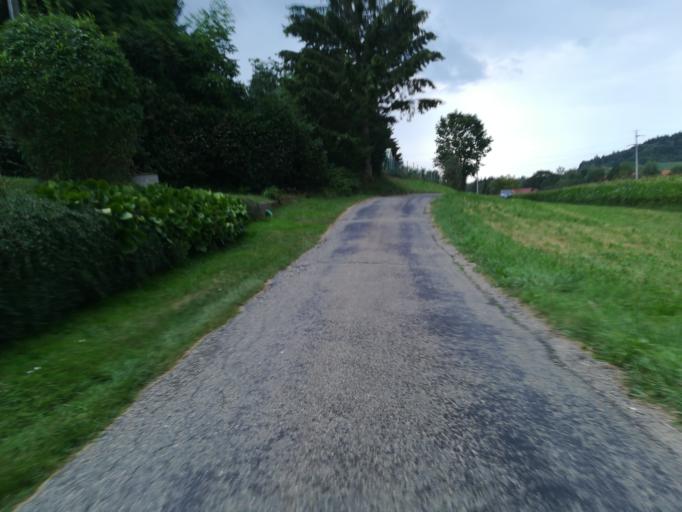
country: DE
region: Baden-Wuerttemberg
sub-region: Freiburg Region
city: Hilzingen
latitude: 47.7587
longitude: 8.8050
